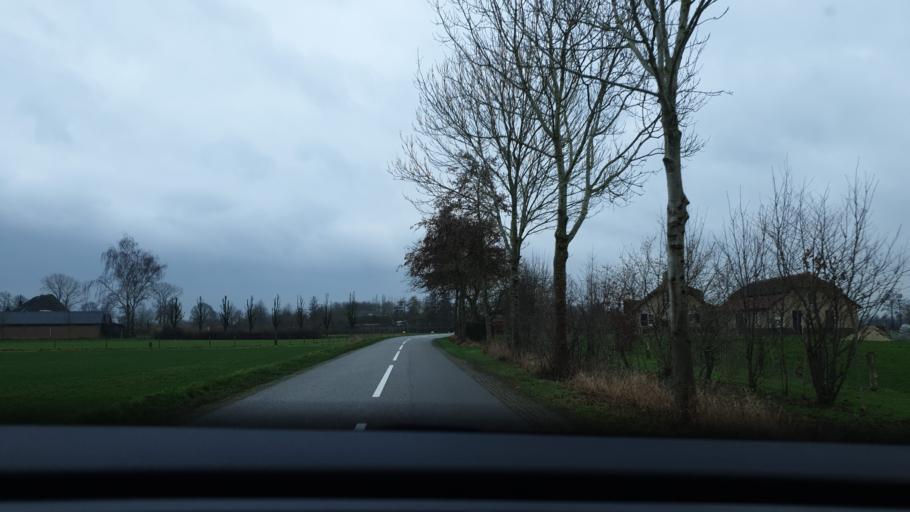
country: NL
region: Gelderland
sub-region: Gemeente Bronckhorst
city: Hengelo
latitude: 52.0369
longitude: 6.2741
